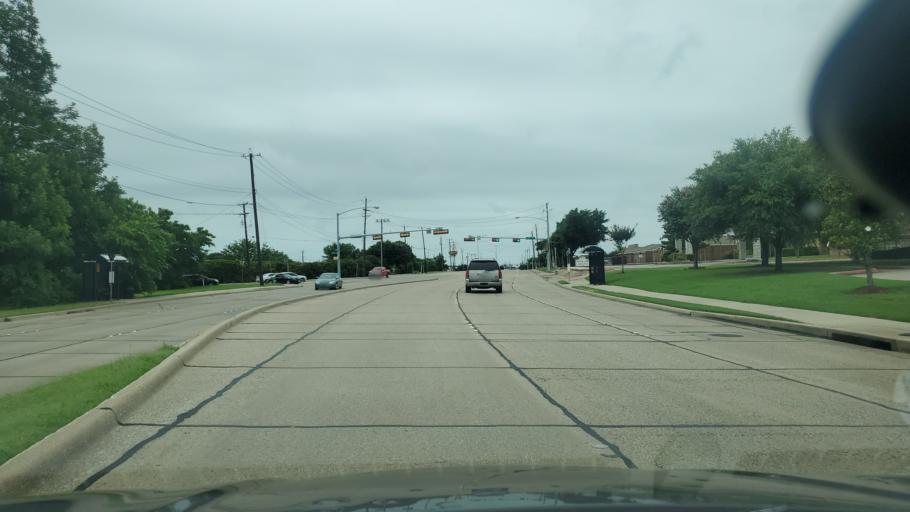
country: US
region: Texas
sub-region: Dallas County
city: Garland
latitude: 32.9345
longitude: -96.6308
